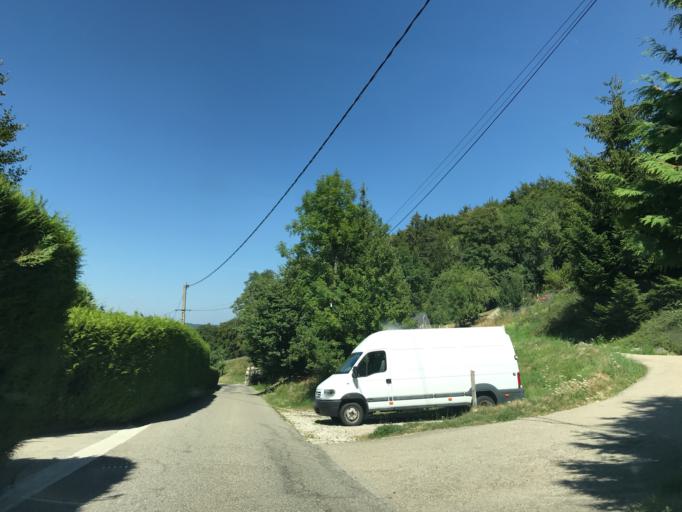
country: FR
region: Rhone-Alpes
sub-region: Departement de la Haute-Savoie
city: Thorens-Glieres
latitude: 45.9725
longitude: 6.2274
